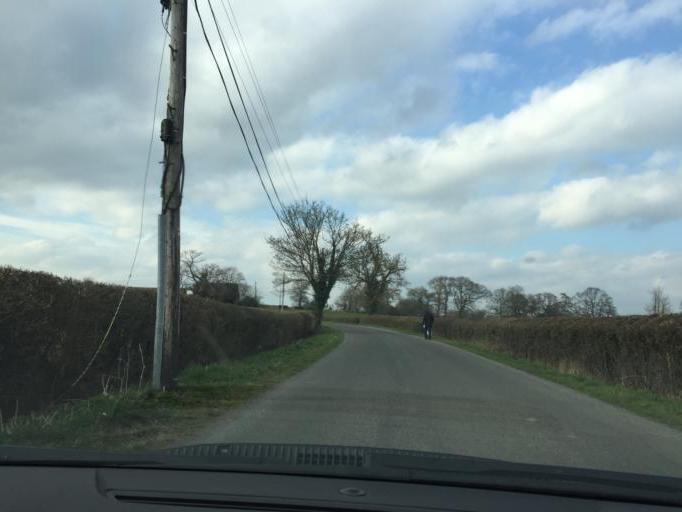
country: GB
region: England
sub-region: Coventry
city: Keresley
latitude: 52.4379
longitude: -1.5706
